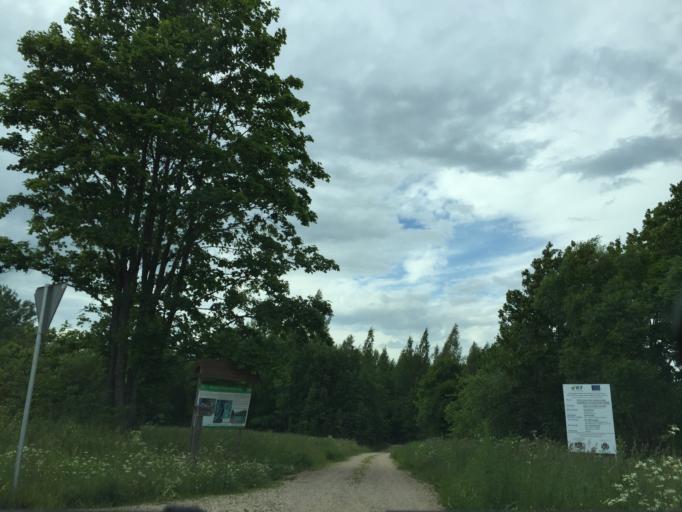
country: LV
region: Apes Novads
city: Ape
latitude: 57.4492
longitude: 26.3491
